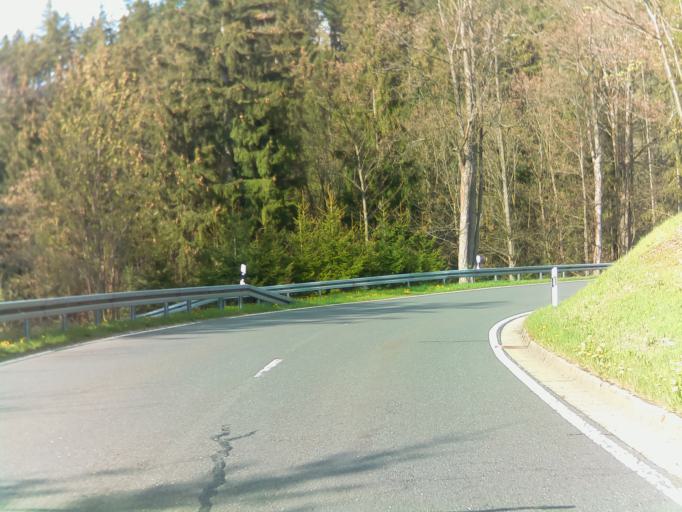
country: DE
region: Thuringia
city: Grafenthal
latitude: 50.5016
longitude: 11.3005
